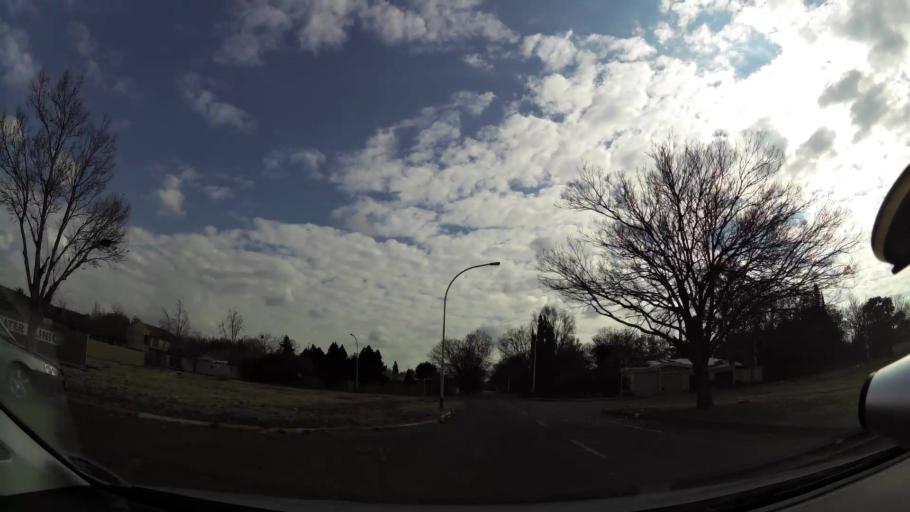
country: ZA
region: Orange Free State
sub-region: Mangaung Metropolitan Municipality
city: Bloemfontein
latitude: -29.0846
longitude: 26.2425
